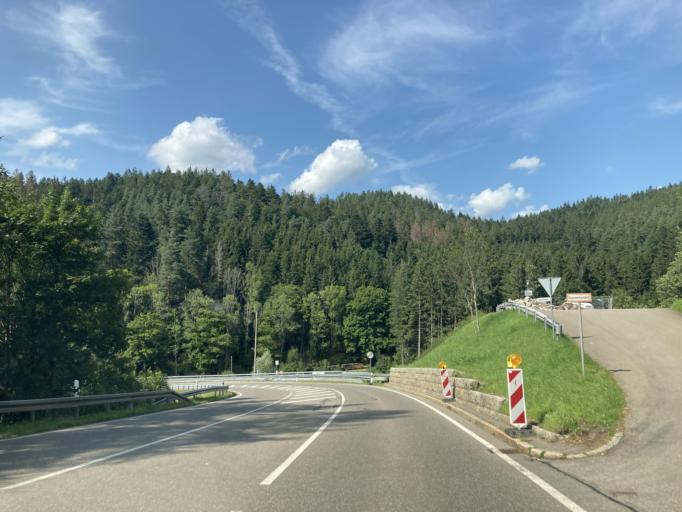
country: DE
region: Baden-Wuerttemberg
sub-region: Freiburg Region
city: Sankt Georgen im Schwarzwald
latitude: 48.1337
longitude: 8.2858
